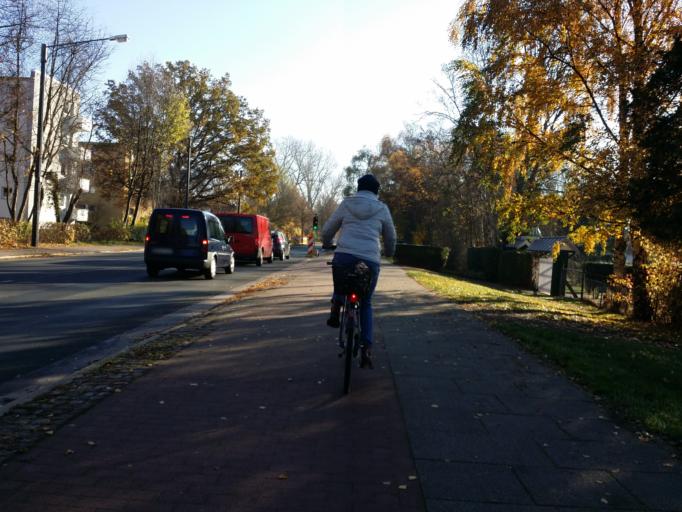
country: DE
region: Bremen
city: Bremen
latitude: 53.0735
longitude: 8.8714
